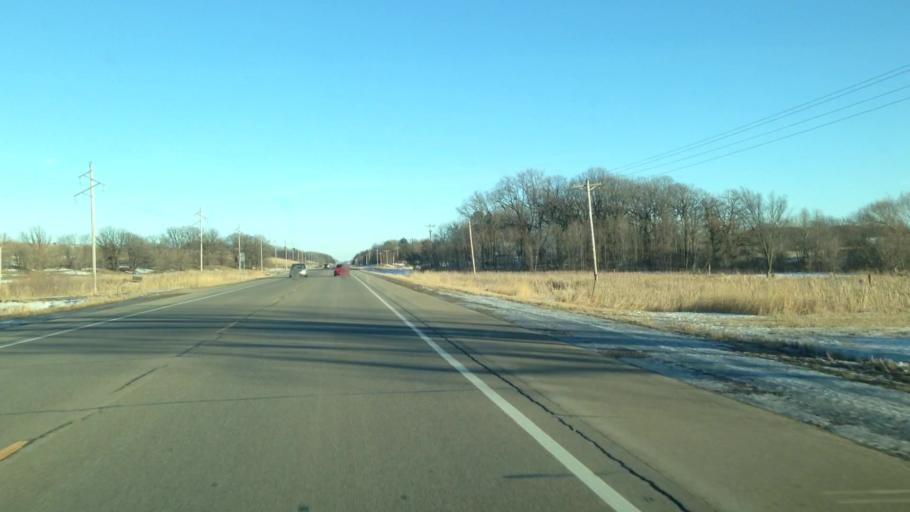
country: US
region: Minnesota
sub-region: Rice County
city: Lonsdale
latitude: 44.4792
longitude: -93.3907
